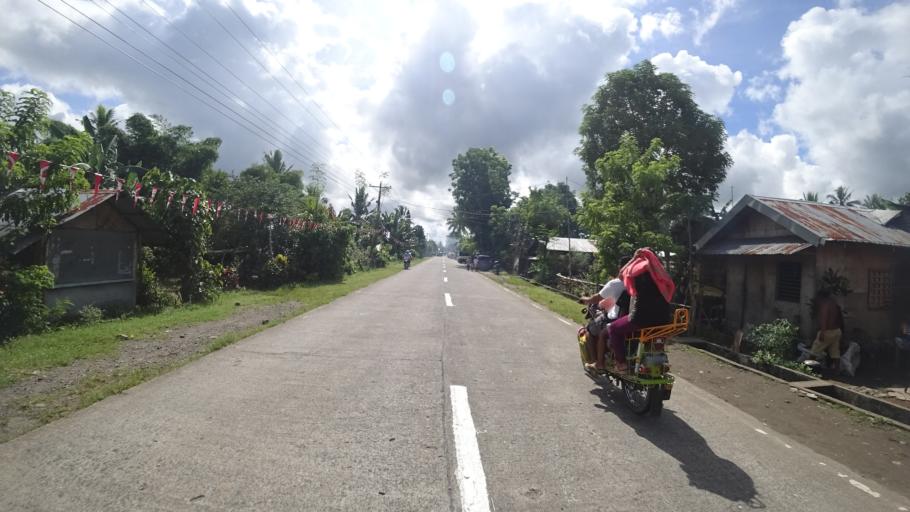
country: PH
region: Eastern Visayas
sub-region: Province of Leyte
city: Burauen
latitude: 10.9802
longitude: 124.9185
